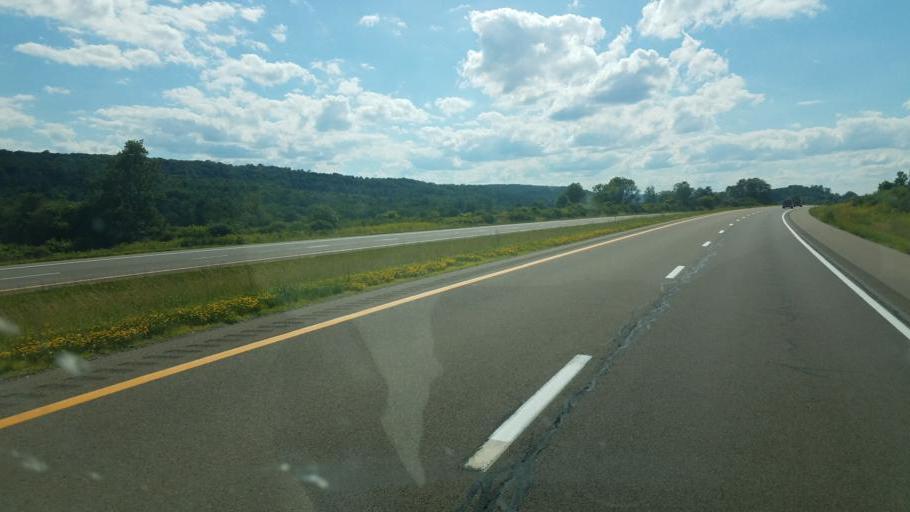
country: US
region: New York
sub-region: Steuben County
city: Hornell
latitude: 42.3685
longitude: -77.6169
